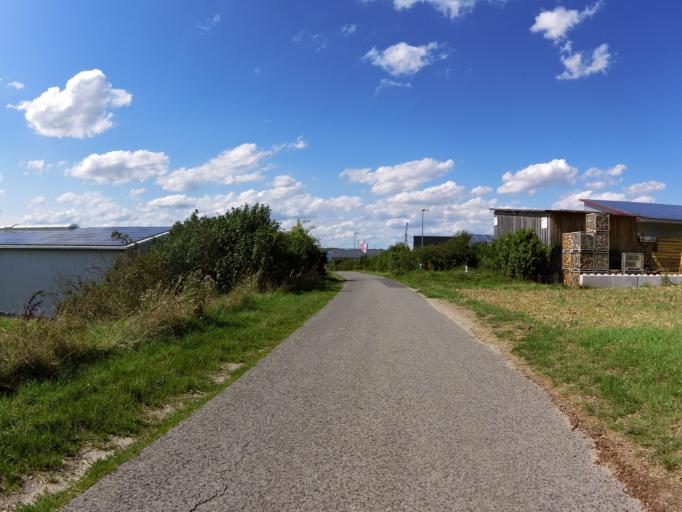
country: DE
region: Bavaria
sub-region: Regierungsbezirk Unterfranken
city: Marktsteft
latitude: 49.6867
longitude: 10.1477
